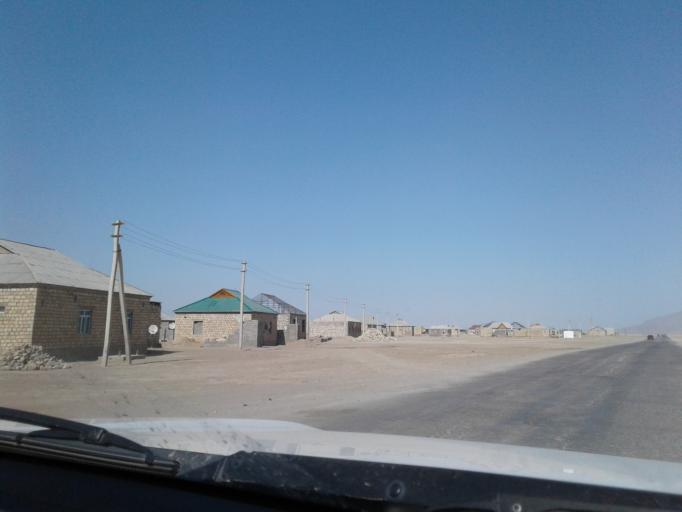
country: TM
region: Balkan
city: Gumdag
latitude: 39.2065
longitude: 54.6227
